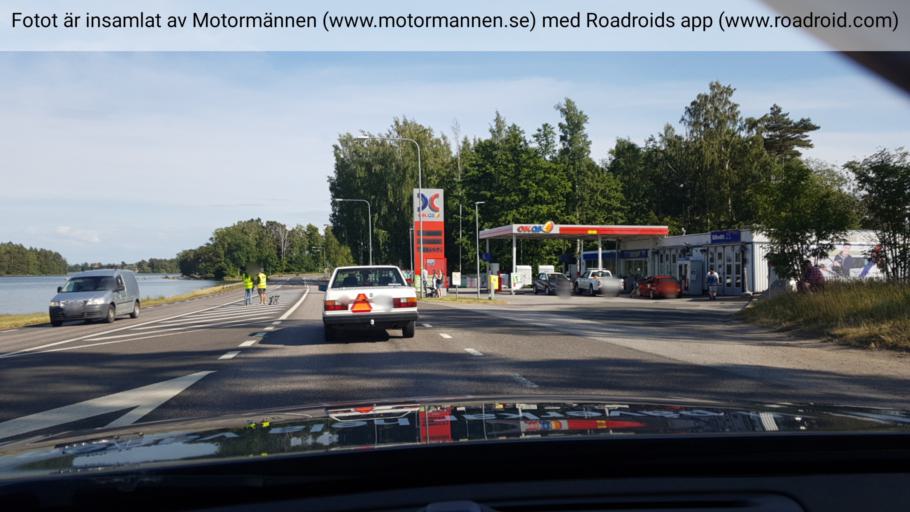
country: SE
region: Vaestra Goetaland
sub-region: Karlsborgs Kommun
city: Karlsborg
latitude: 58.5449
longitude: 14.5021
